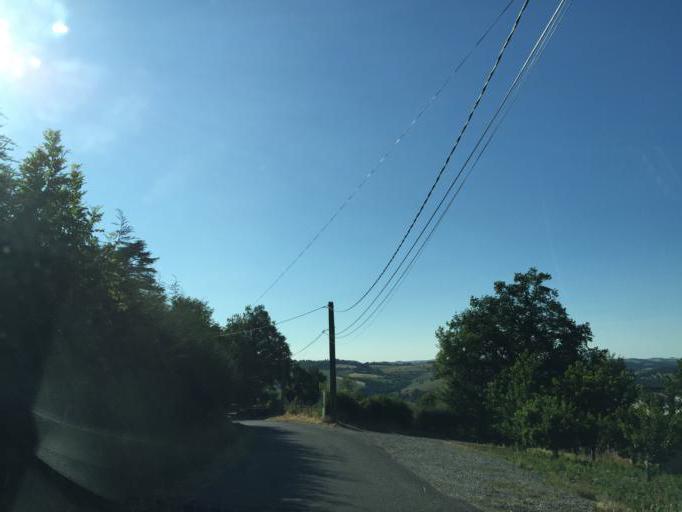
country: FR
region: Rhone-Alpes
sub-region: Departement de la Loire
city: Saint-Jean-Bonnefonds
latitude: 45.4459
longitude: 4.4928
